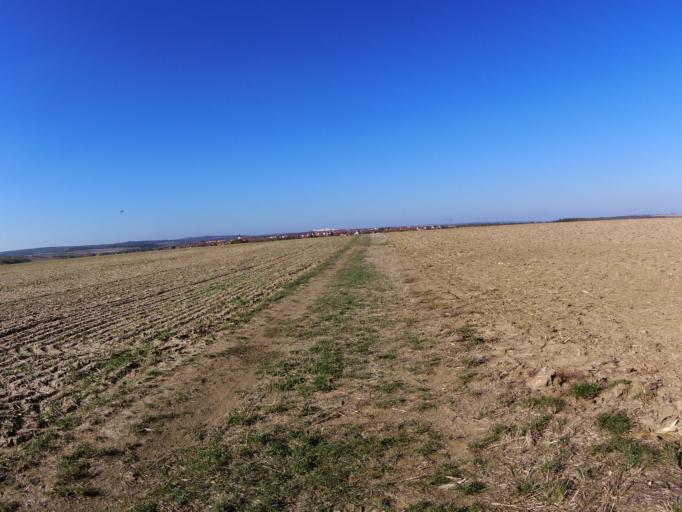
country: DE
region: Bavaria
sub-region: Regierungsbezirk Unterfranken
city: Eibelstadt
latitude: 49.7099
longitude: 9.9759
